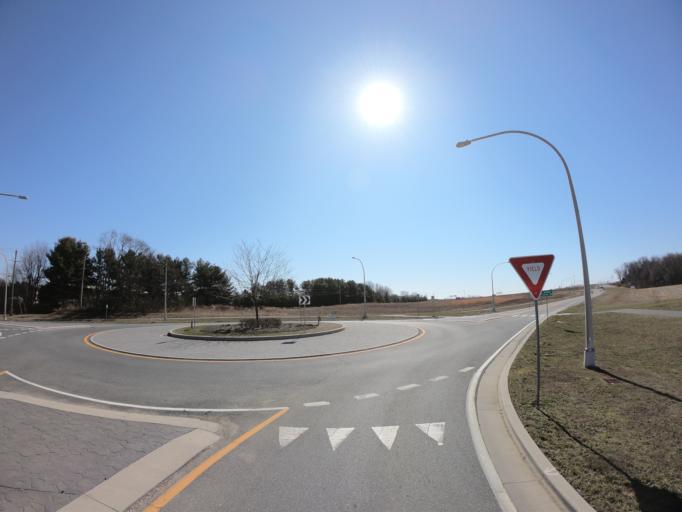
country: US
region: Delaware
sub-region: New Castle County
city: Middletown
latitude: 39.5302
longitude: -75.6785
